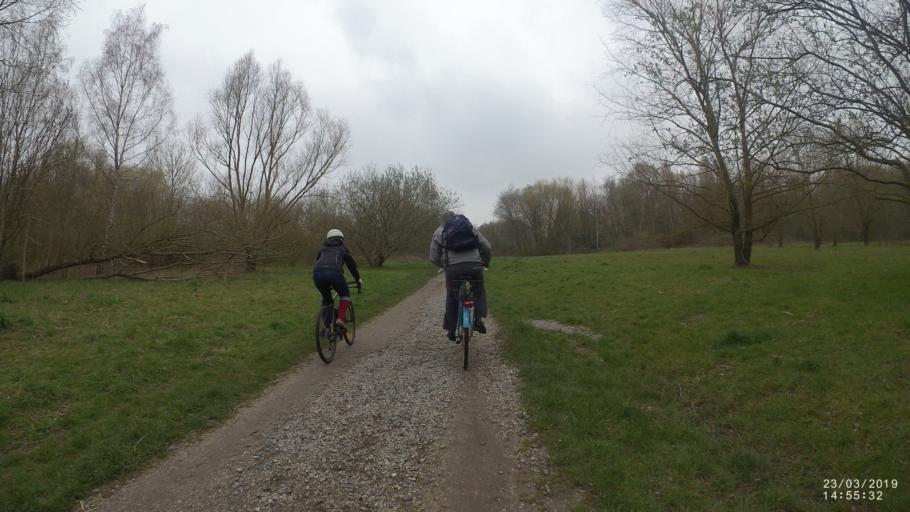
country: BE
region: Flanders
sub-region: Provincie Vlaams-Brabant
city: Dilbeek
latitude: 50.8530
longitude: 4.2945
